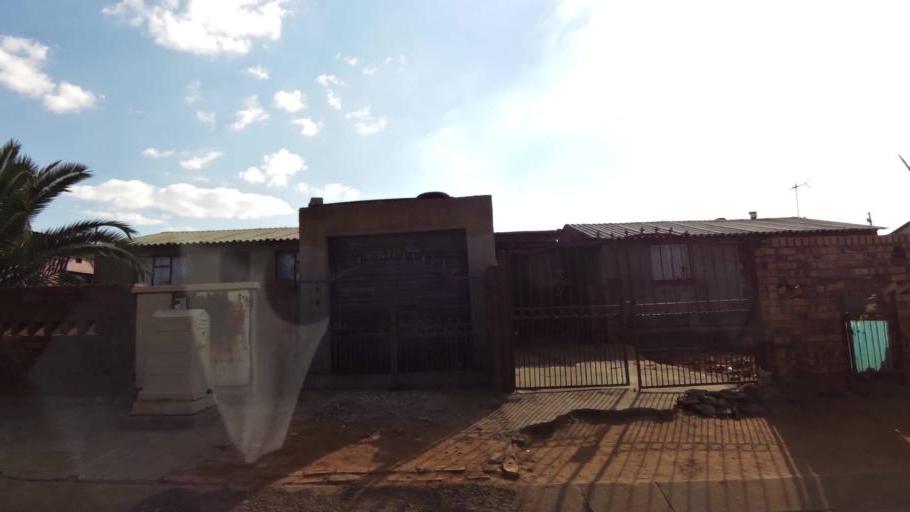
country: ZA
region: Gauteng
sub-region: City of Johannesburg Metropolitan Municipality
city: Soweto
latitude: -26.2294
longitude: 27.8817
